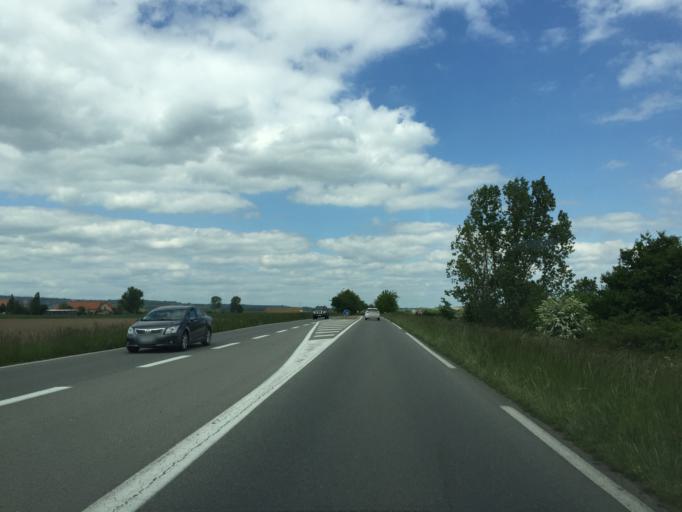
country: FR
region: Auvergne
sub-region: Departement du Puy-de-Dome
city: Aigueperse
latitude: 45.9766
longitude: 3.1806
